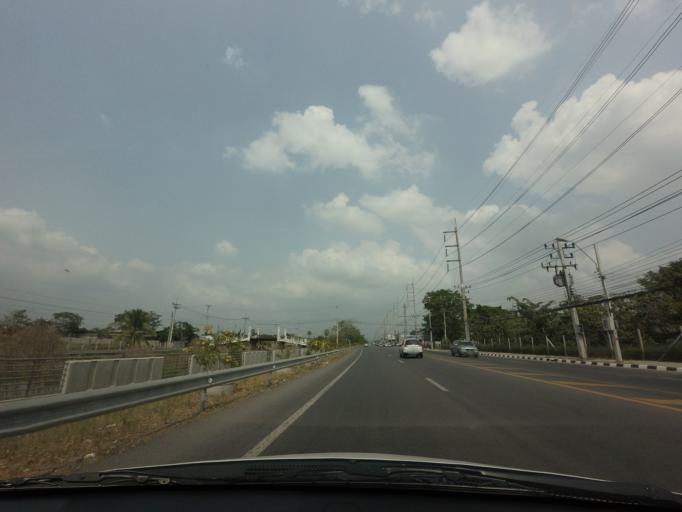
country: TH
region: Pathum Thani
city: Thanyaburi
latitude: 14.0536
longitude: 100.7102
